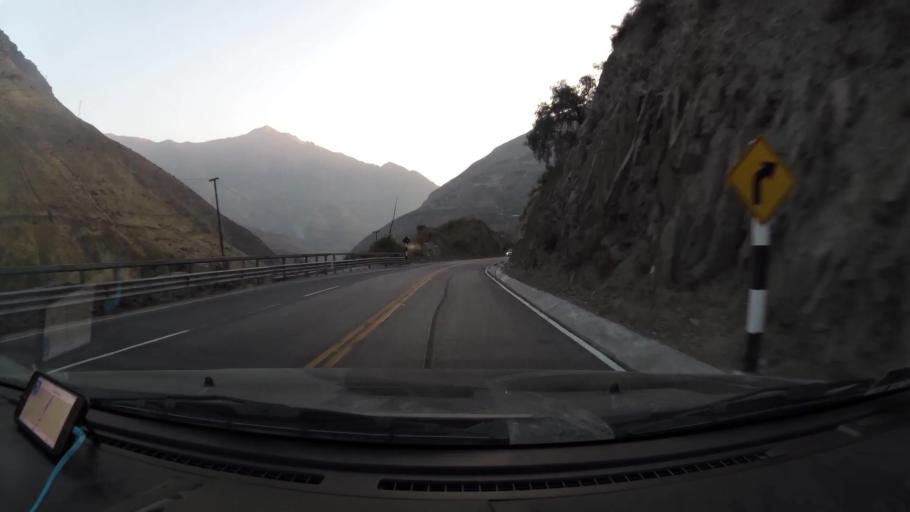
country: PE
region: Lima
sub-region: Provincia de Huarochiri
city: Matucana
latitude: -11.8589
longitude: -76.4168
